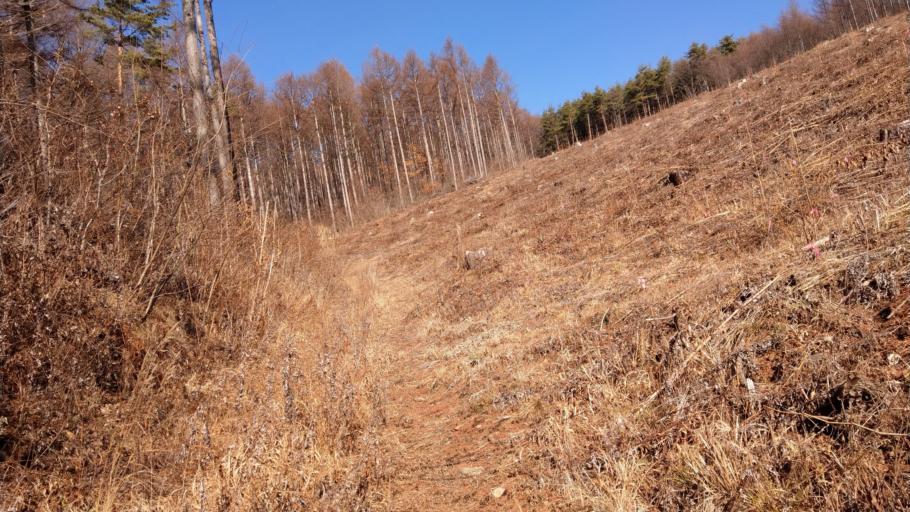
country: JP
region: Nagano
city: Komoro
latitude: 36.3751
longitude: 138.4377
